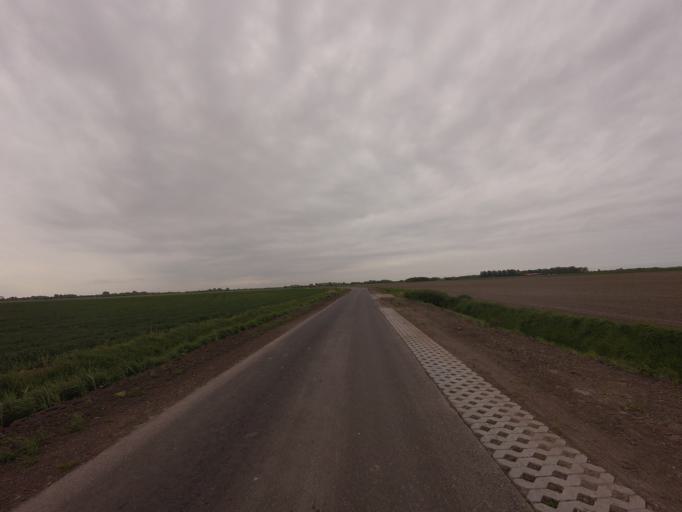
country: NL
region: Zeeland
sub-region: Gemeente Middelburg
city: Middelburg
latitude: 51.5481
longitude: 3.5453
